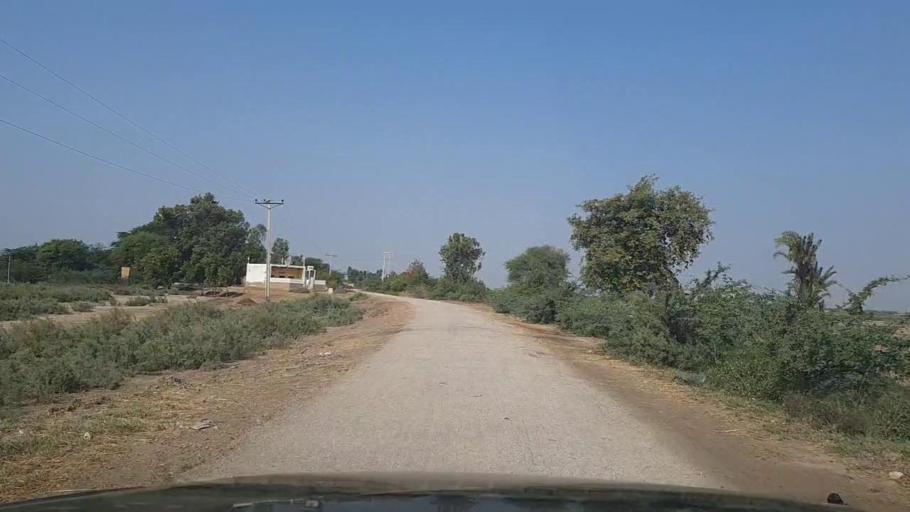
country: PK
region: Sindh
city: Thatta
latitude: 24.6117
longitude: 67.8229
